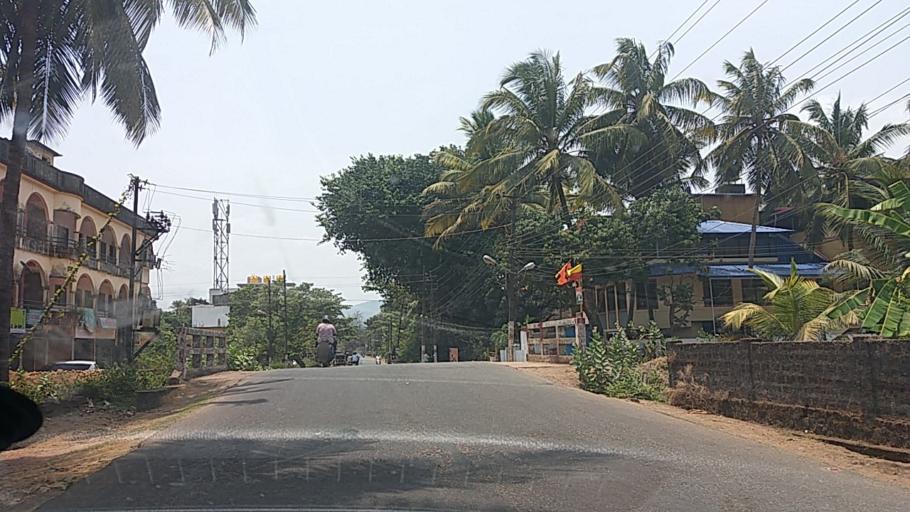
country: IN
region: Karnataka
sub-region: Uttar Kannada
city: Karwar
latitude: 14.8114
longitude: 74.1461
